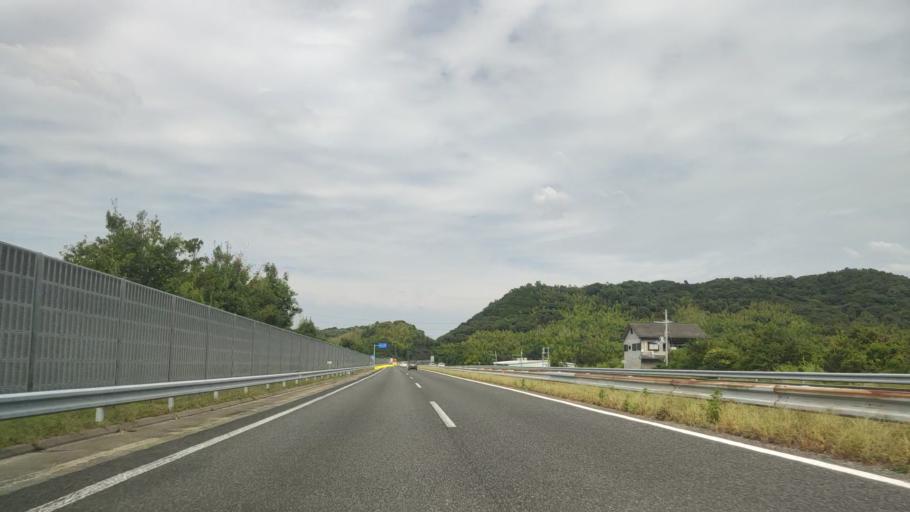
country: JP
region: Wakayama
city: Kainan
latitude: 34.1761
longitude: 135.2357
